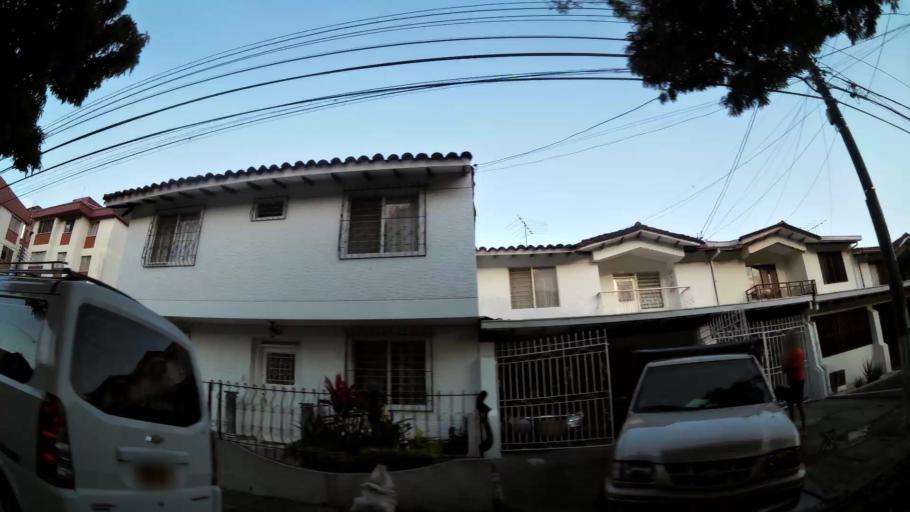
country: CO
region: Valle del Cauca
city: Cali
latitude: 3.4059
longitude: -76.5552
